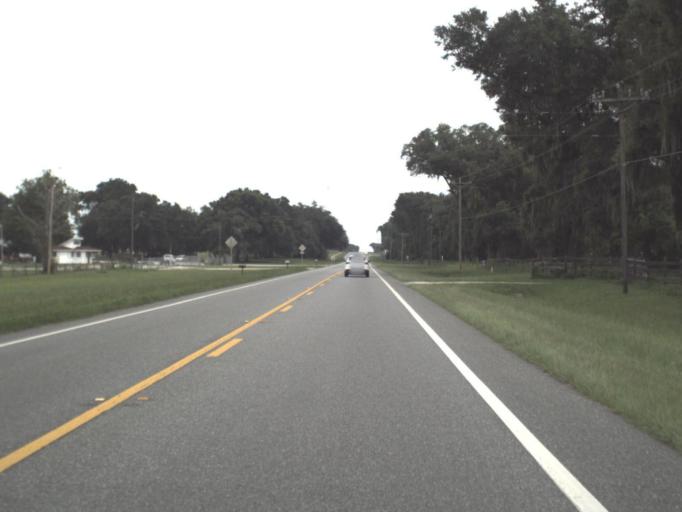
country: US
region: Florida
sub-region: Columbia County
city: Watertown
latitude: 30.0973
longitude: -82.6033
